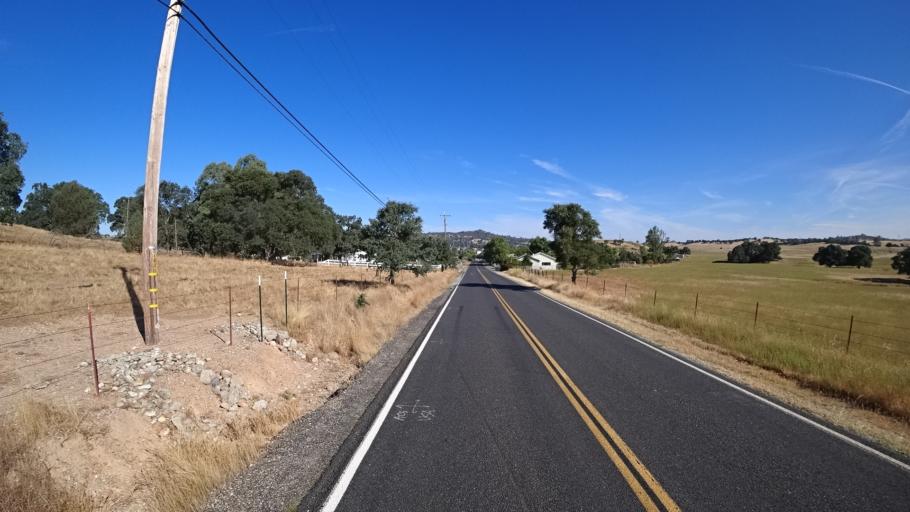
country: US
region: California
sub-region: Calaveras County
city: Valley Springs
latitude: 38.1823
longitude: -120.8155
